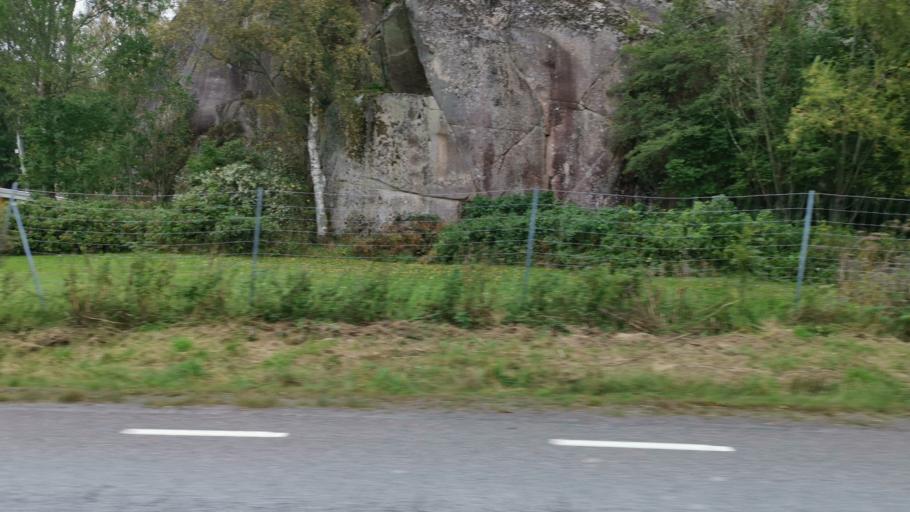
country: SE
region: Vaestra Goetaland
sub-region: Lysekils Kommun
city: Brastad
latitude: 58.5624
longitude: 11.4726
